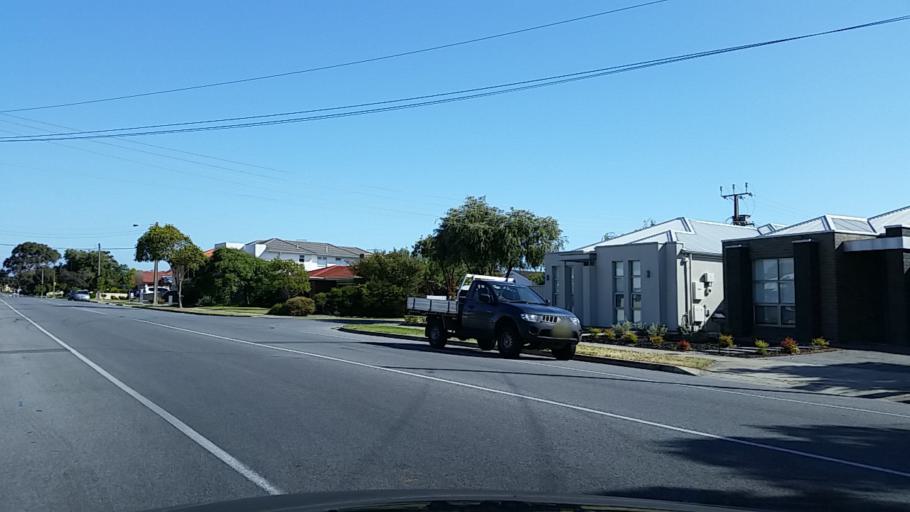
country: AU
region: South Australia
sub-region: Charles Sturt
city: Henley Beach
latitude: -34.9174
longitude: 138.5029
